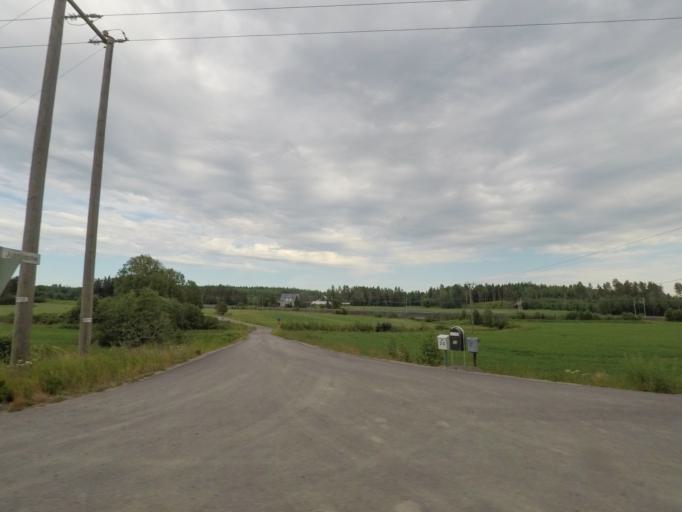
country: FI
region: Uusimaa
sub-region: Helsinki
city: Maentsaelae
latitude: 60.6858
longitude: 25.3694
